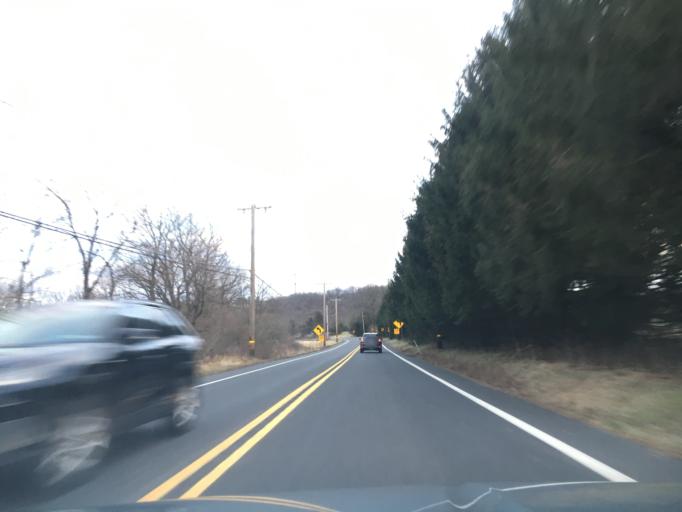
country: US
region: Pennsylvania
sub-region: Lehigh County
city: Schnecksville
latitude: 40.6776
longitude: -75.6451
